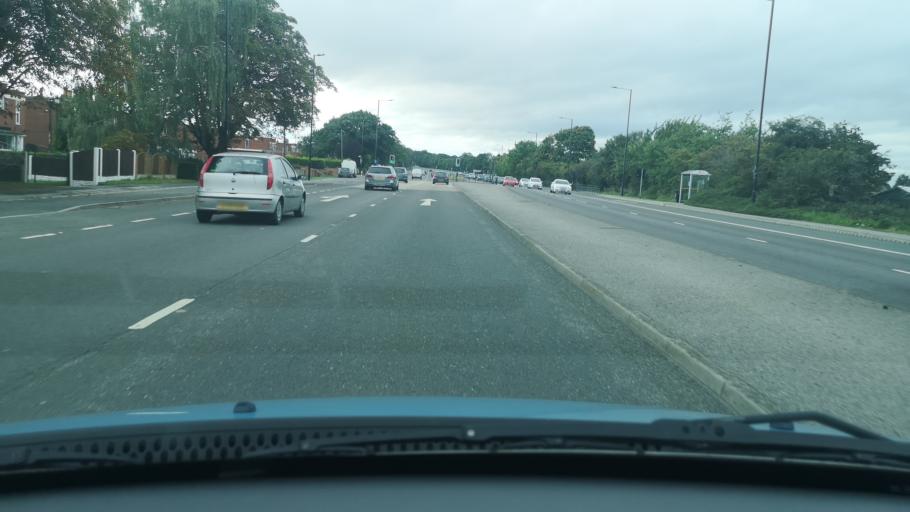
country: GB
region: England
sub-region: Doncaster
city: Bentley
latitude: 53.5392
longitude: -1.1669
